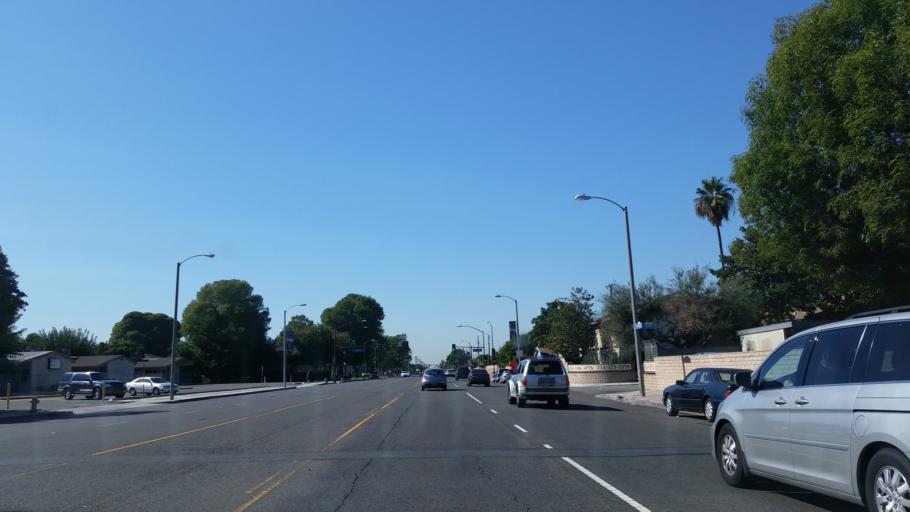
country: US
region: California
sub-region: Orange County
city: Buena Park
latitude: 33.8466
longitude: -118.0051
